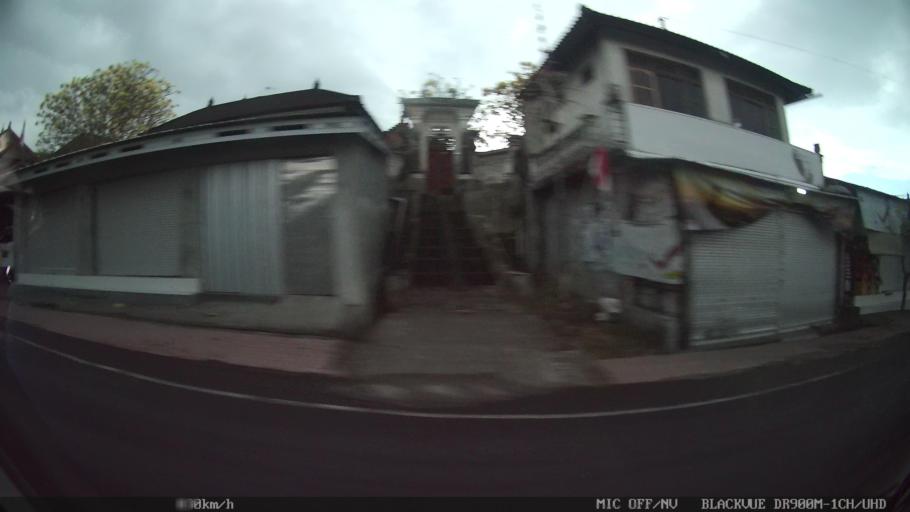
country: ID
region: Bali
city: Banjar Pasekan
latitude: -8.6075
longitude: 115.2834
